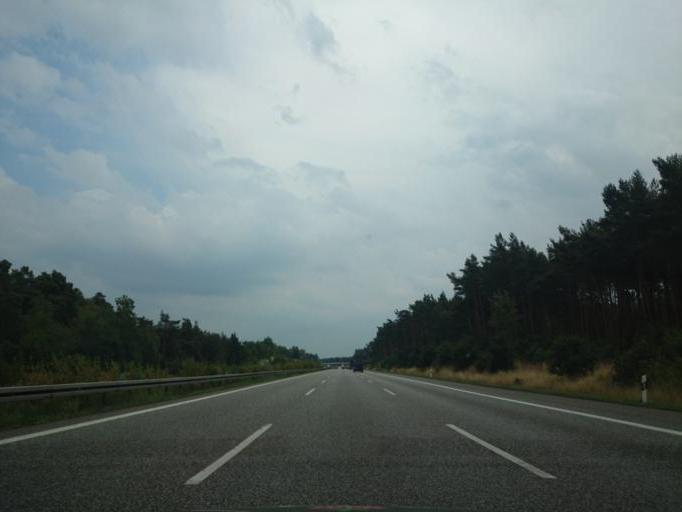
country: DE
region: Brandenburg
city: Ludwigsfelde
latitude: 52.3009
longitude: 13.2335
